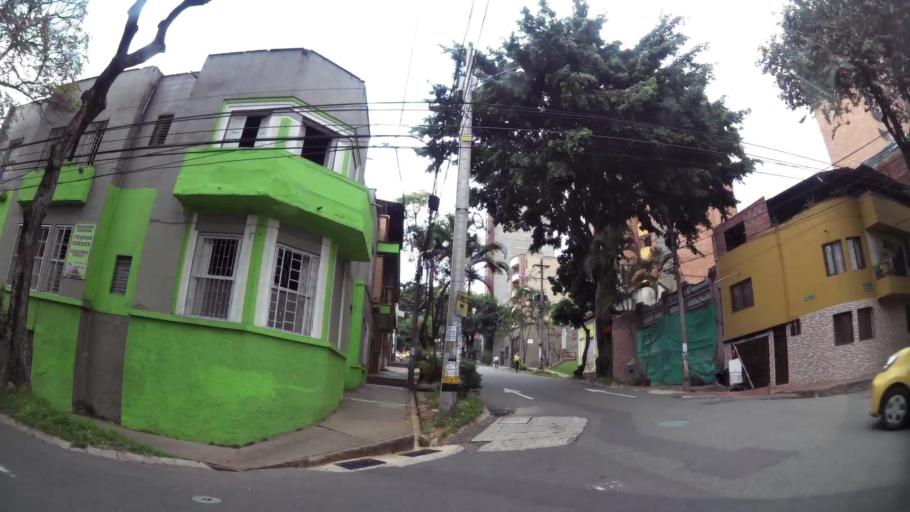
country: CO
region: Antioquia
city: Medellin
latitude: 6.2559
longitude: -75.5608
